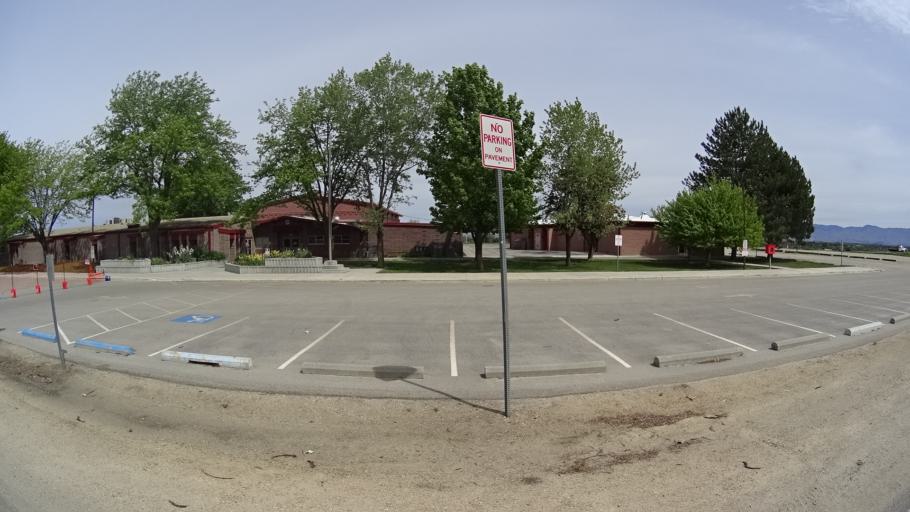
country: US
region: Idaho
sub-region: Ada County
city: Meridian
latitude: 43.5612
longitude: -116.3808
